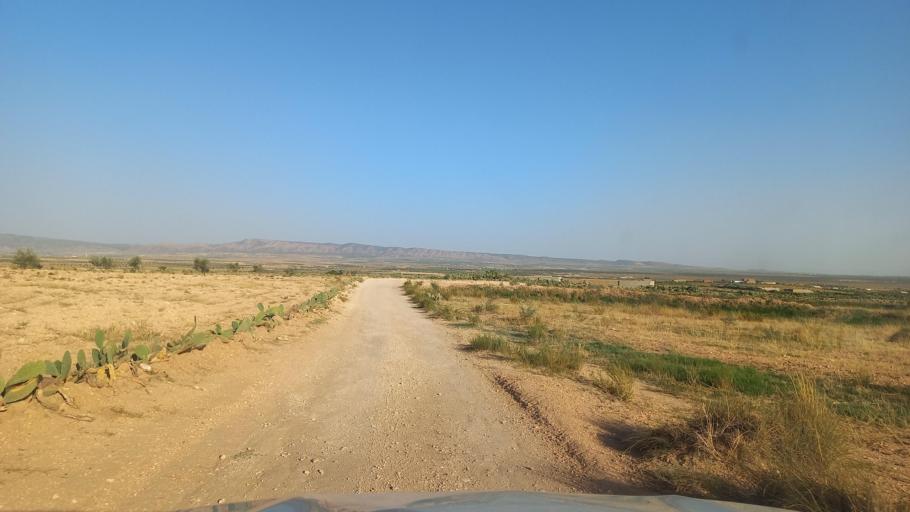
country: TN
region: Al Qasrayn
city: Sbiba
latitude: 35.3673
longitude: 9.0104
